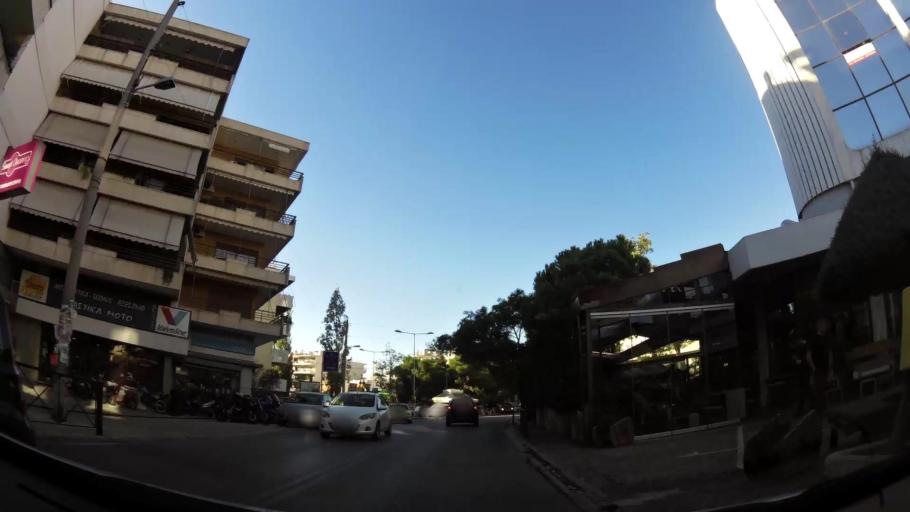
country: GR
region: Attica
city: Pefki
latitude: 38.0594
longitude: 23.7981
